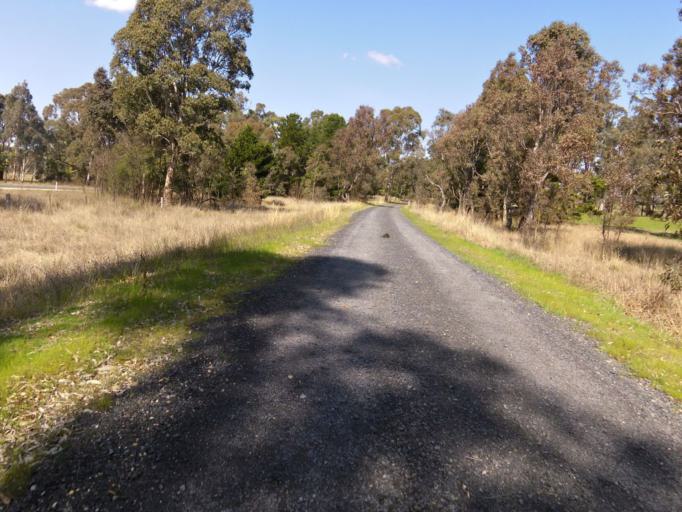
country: AU
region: Victoria
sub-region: Murrindindi
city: Alexandra
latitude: -36.9891
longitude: 145.7356
